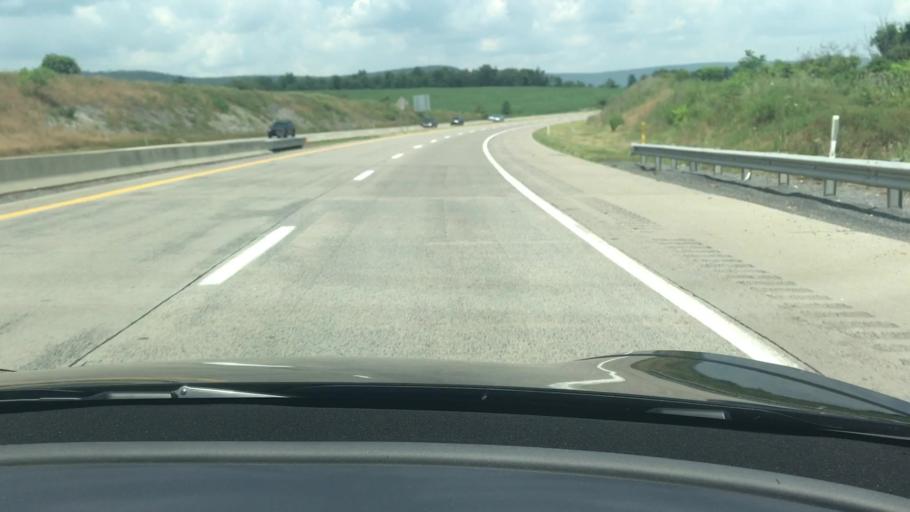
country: US
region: Pennsylvania
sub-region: Mifflin County
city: Church Hill
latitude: 40.6826
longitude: -77.6077
